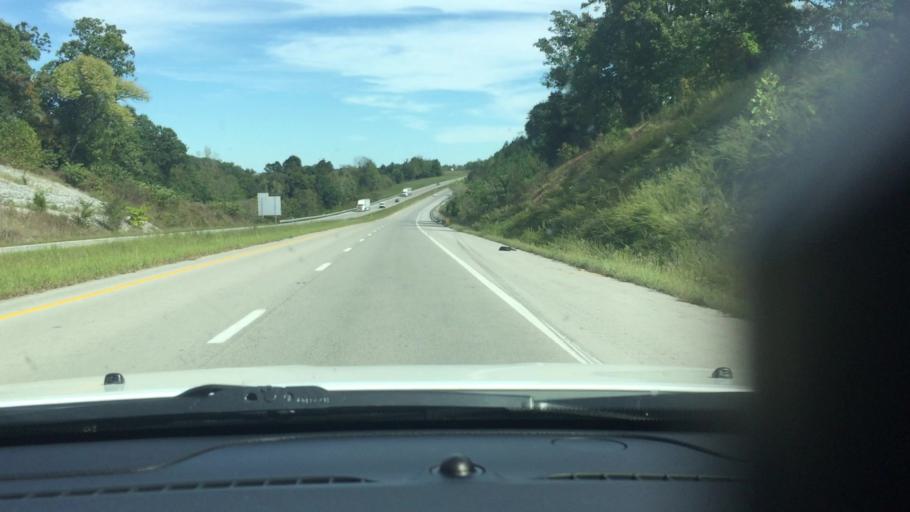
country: US
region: Kentucky
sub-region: Caldwell County
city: Princeton
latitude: 37.1406
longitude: -87.8270
